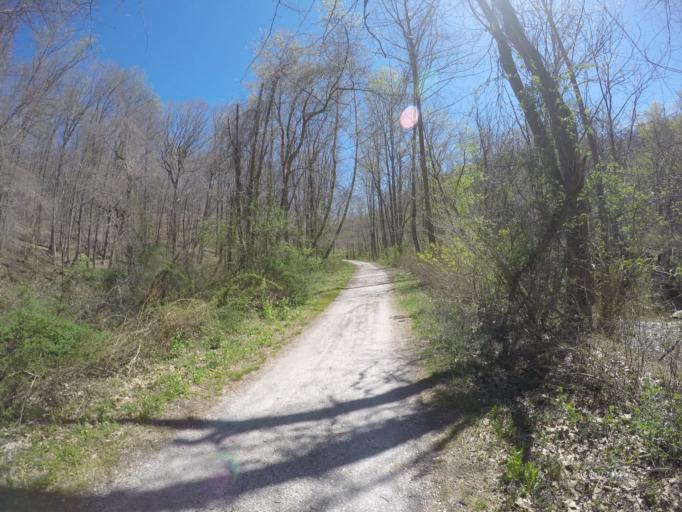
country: US
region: Maryland
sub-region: Baltimore County
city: Hunt Valley
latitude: 39.5991
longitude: -76.6249
